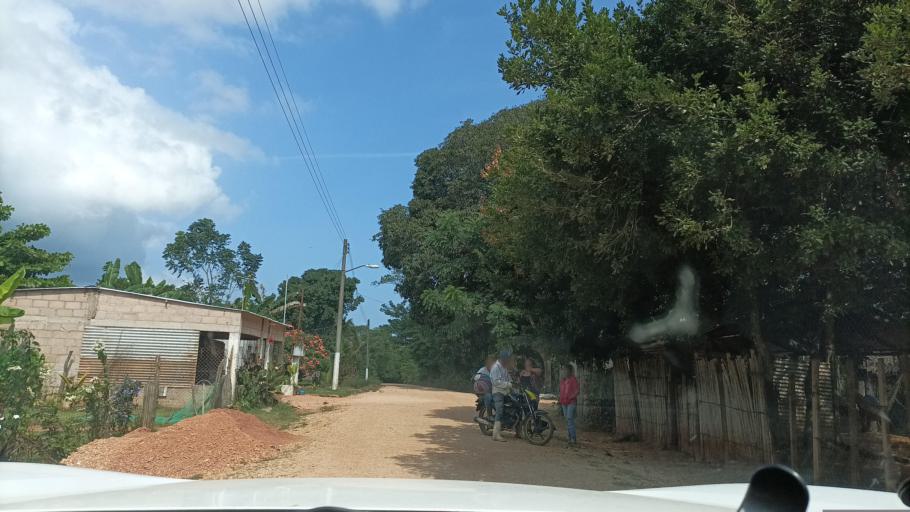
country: MX
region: Veracruz
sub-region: Chinameca
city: Chacalapa
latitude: 18.0822
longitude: -94.6726
